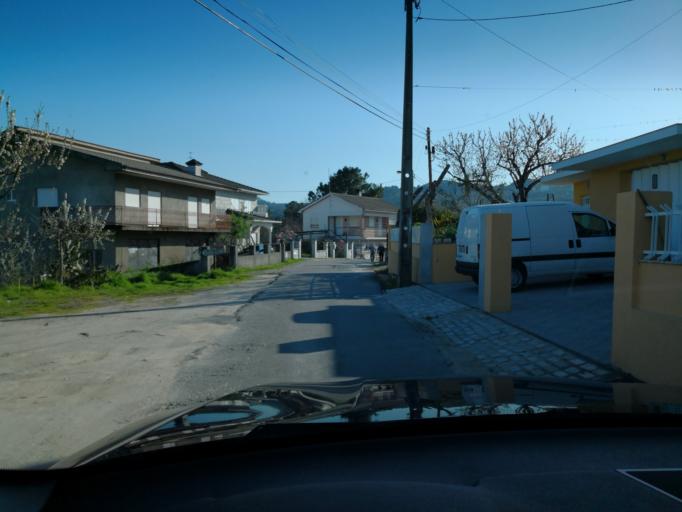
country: PT
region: Vila Real
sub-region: Vila Real
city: Vila Real
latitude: 41.2866
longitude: -7.7824
